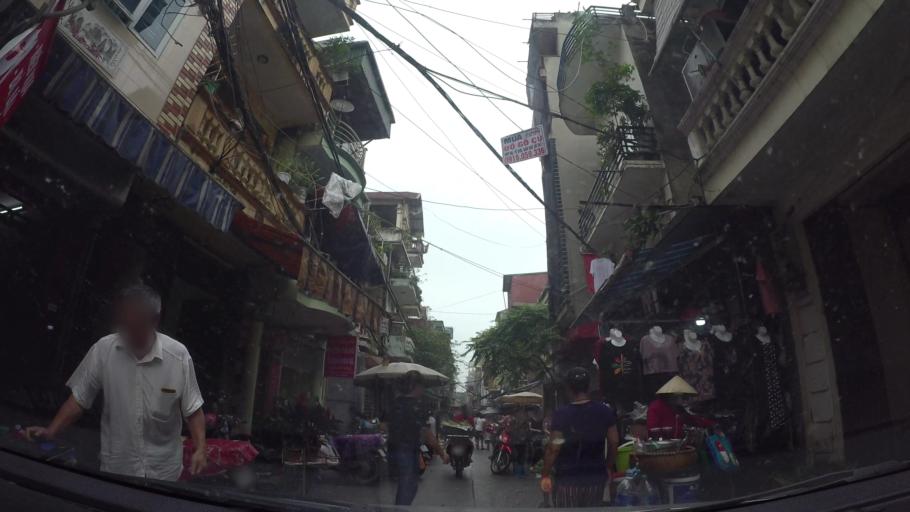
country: VN
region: Ha Noi
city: Hoan Kiem
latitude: 21.0378
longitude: 105.8552
